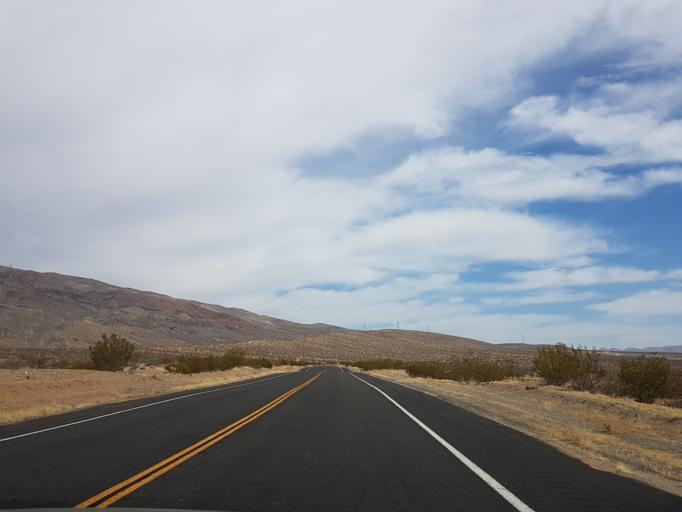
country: US
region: California
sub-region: Kern County
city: Ridgecrest
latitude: 35.4232
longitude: -117.7308
